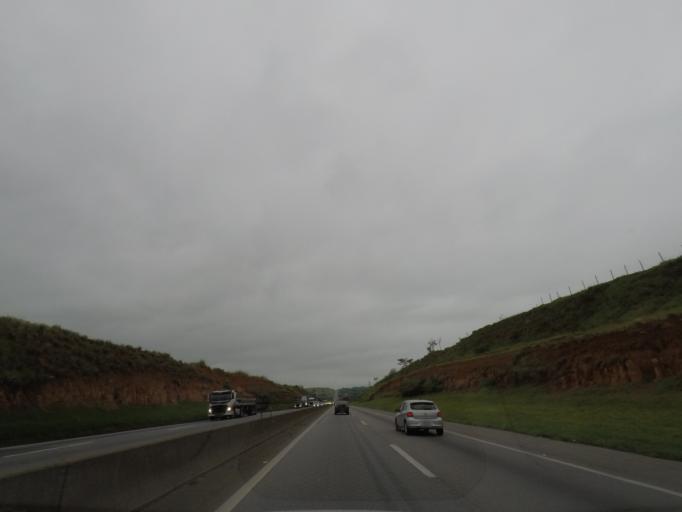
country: BR
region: Sao Paulo
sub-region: Taubate
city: Taubate
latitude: -23.0056
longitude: -45.5109
